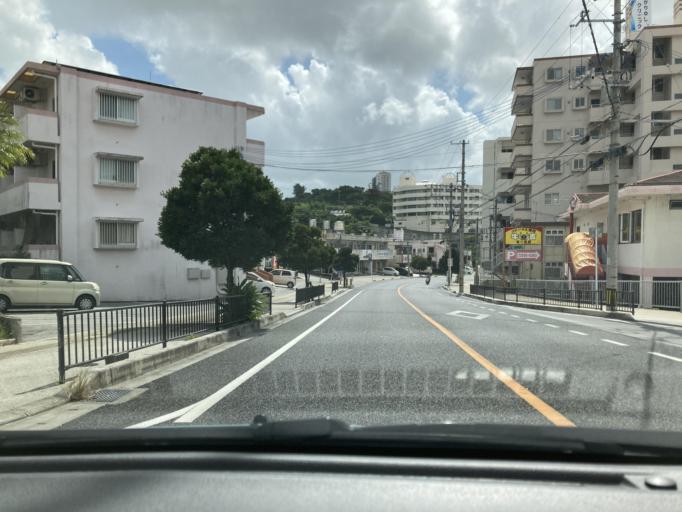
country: JP
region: Okinawa
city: Ginowan
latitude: 26.2623
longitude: 127.7294
